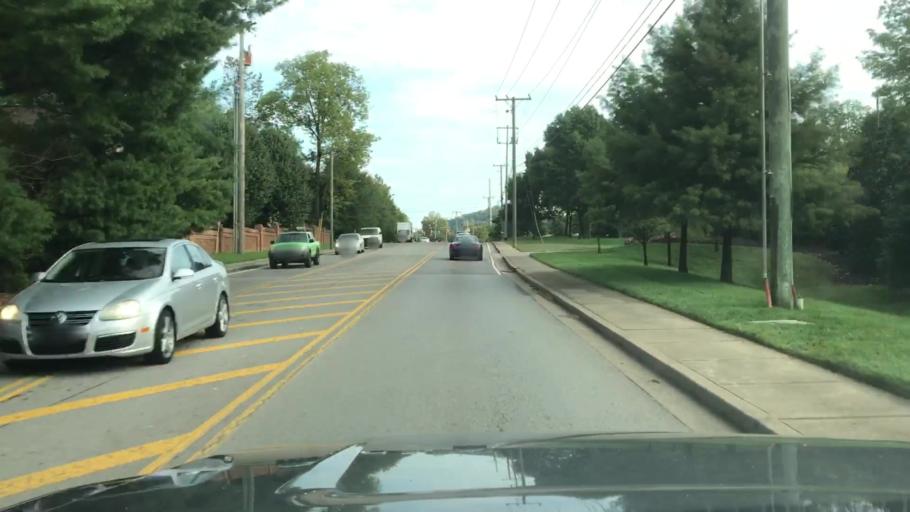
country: US
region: Tennessee
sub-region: Williamson County
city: Brentwood
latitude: 36.0378
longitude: -86.8167
